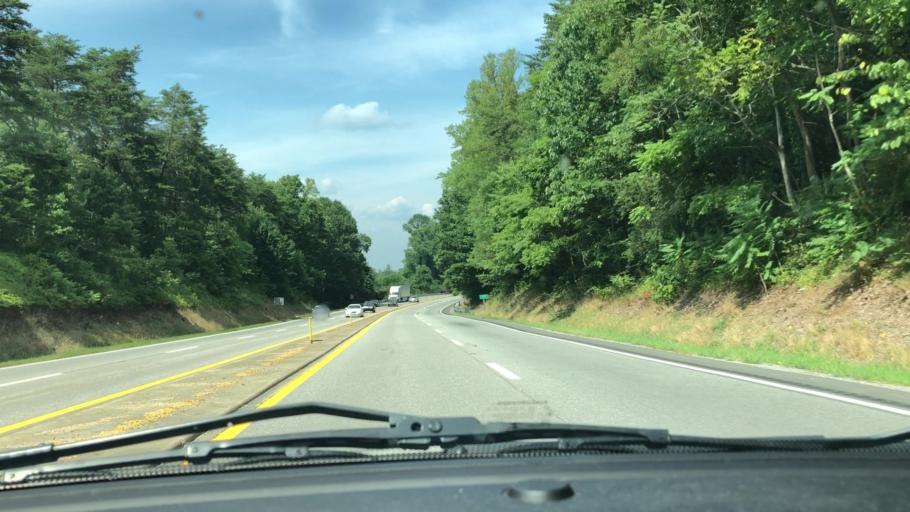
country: US
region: Virginia
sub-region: Henry County
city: Horse Pasture
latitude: 36.5746
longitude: -79.8688
